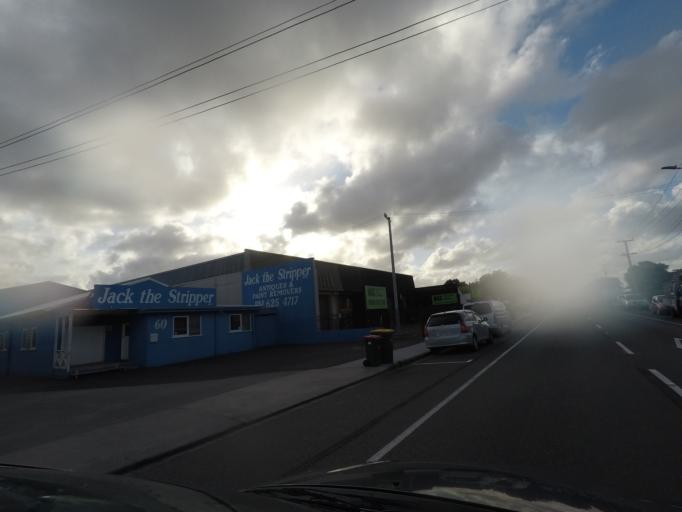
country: NZ
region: Auckland
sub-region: Auckland
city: Auckland
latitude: -36.9128
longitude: 174.7506
